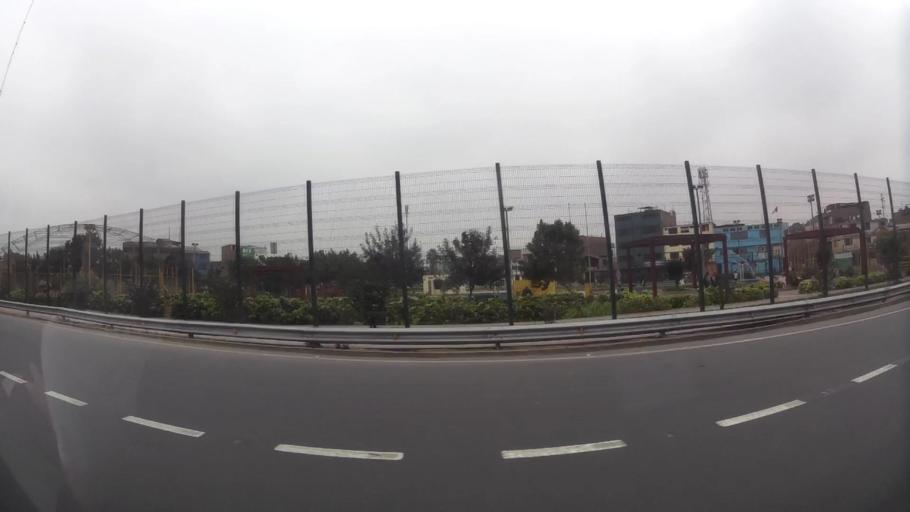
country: PE
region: Lima
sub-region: Lima
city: San Luis
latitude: -12.0481
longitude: -76.9800
